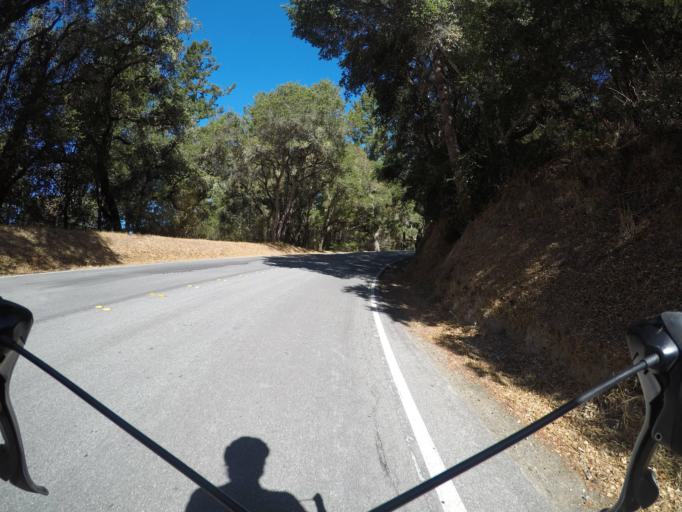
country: US
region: California
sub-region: San Mateo County
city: Portola Valley
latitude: 37.2917
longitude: -122.2788
